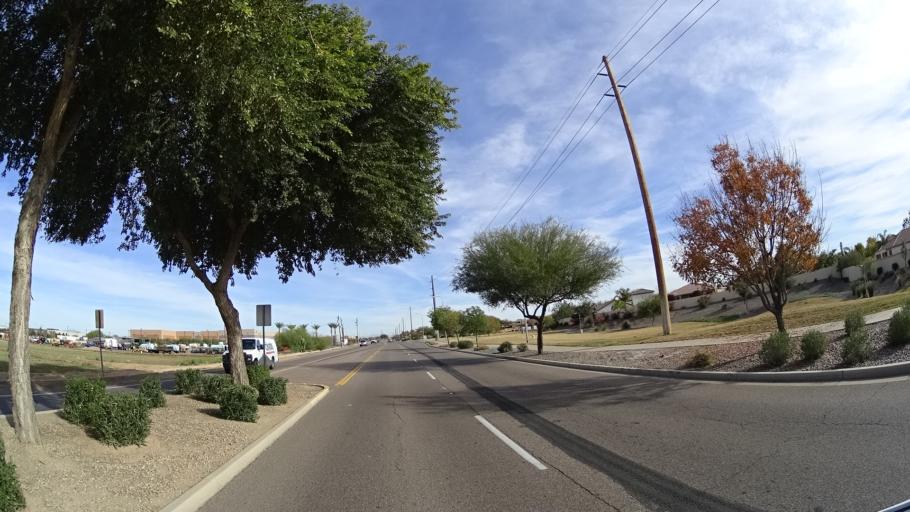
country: US
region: Arizona
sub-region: Maricopa County
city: Chandler
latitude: 33.2627
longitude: -111.8002
